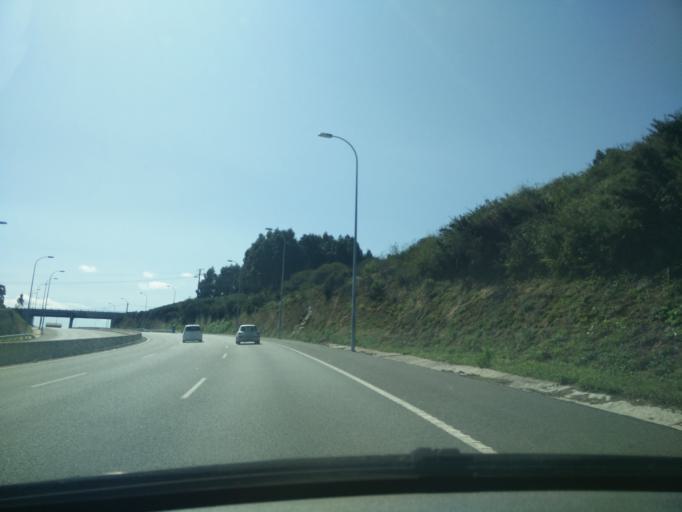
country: ES
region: Galicia
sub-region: Provincia da Coruna
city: A Coruna
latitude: 43.3631
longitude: -8.4327
